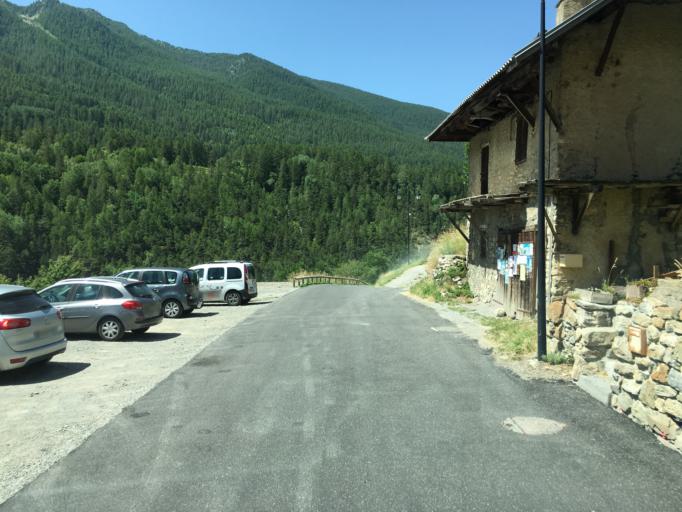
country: FR
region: Provence-Alpes-Cote d'Azur
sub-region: Departement des Hautes-Alpes
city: Embrun
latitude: 44.5494
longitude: 6.5961
